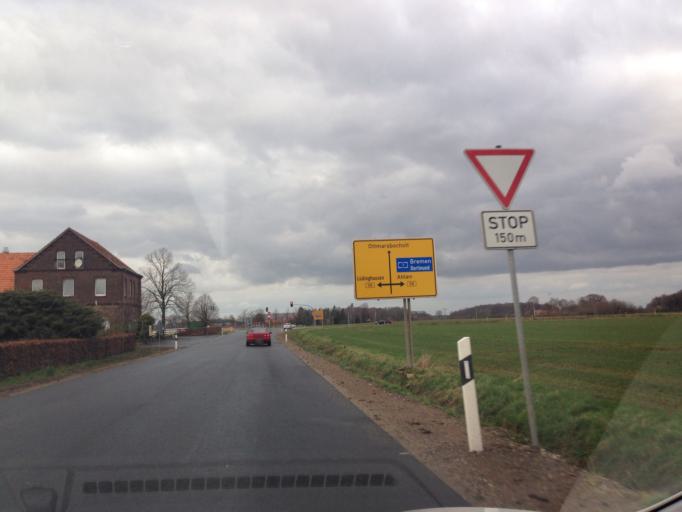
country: DE
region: North Rhine-Westphalia
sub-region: Regierungsbezirk Munster
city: Nordkirchen
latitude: 51.7851
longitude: 7.5423
